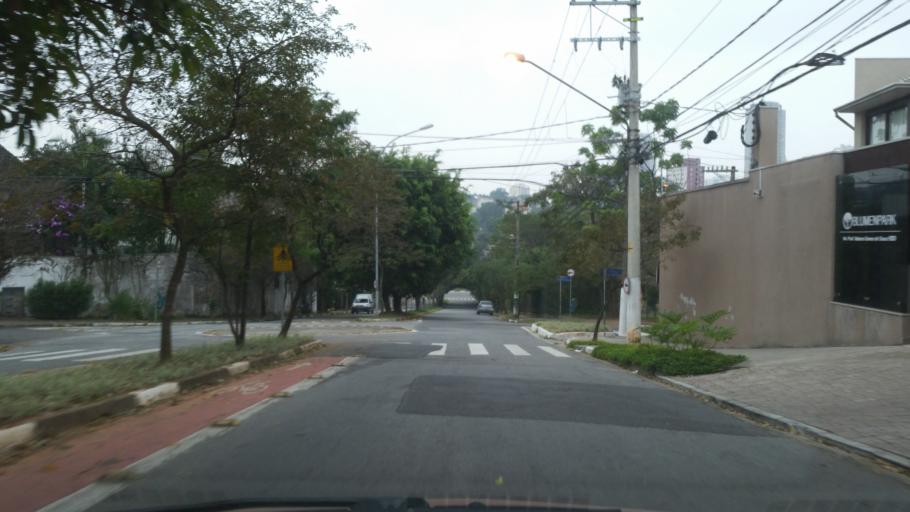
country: BR
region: Sao Paulo
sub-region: Diadema
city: Diadema
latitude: -23.6397
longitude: -46.6787
